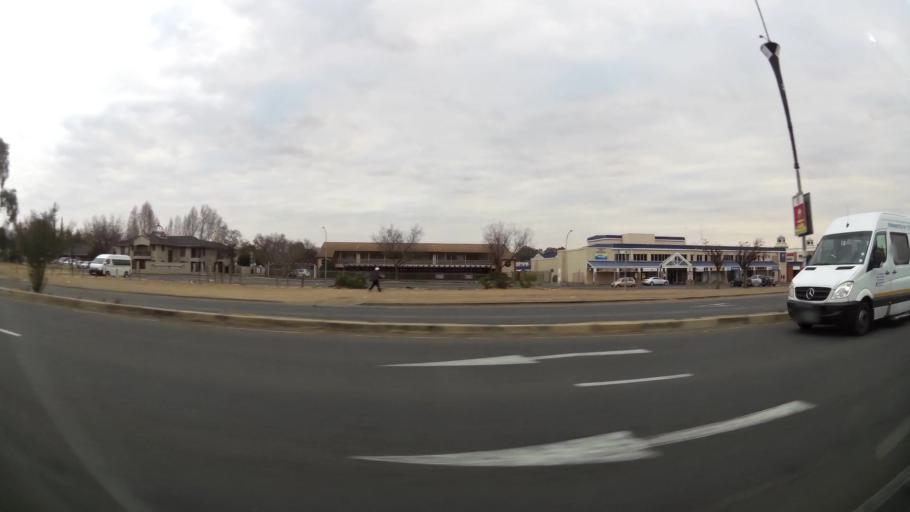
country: ZA
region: Orange Free State
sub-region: Mangaung Metropolitan Municipality
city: Bloemfontein
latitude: -29.1082
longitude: 26.1974
